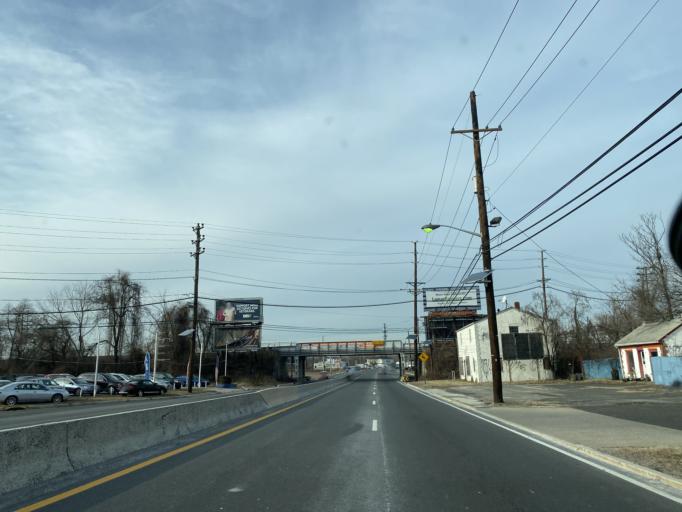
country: US
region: New Jersey
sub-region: Burlington County
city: Palmyra
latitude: 39.9964
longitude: -75.0326
